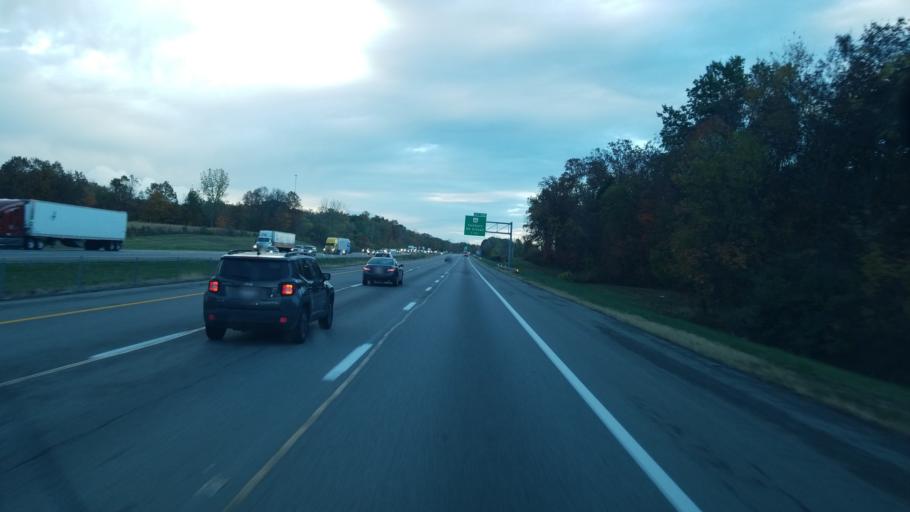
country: US
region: Ohio
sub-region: Morrow County
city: Cardington
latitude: 40.3920
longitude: -82.8236
